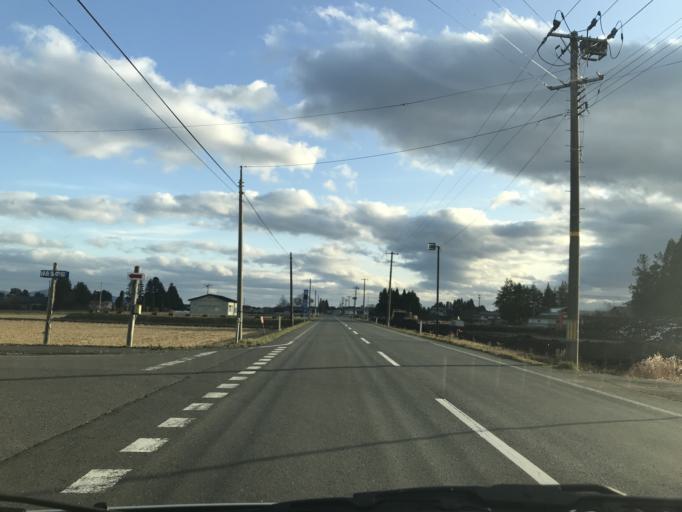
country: JP
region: Iwate
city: Mizusawa
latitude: 39.1383
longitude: 141.0510
